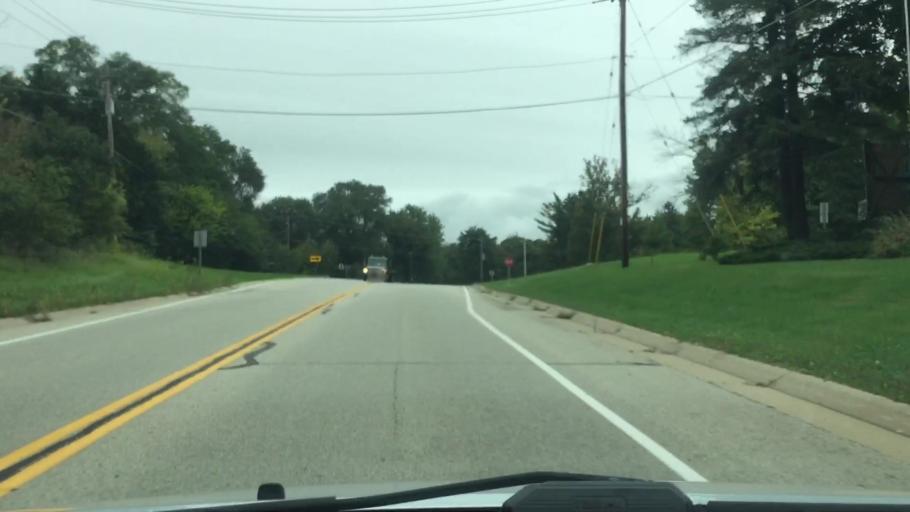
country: US
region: Wisconsin
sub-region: Walworth County
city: Elkhorn
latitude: 42.7650
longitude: -88.5546
